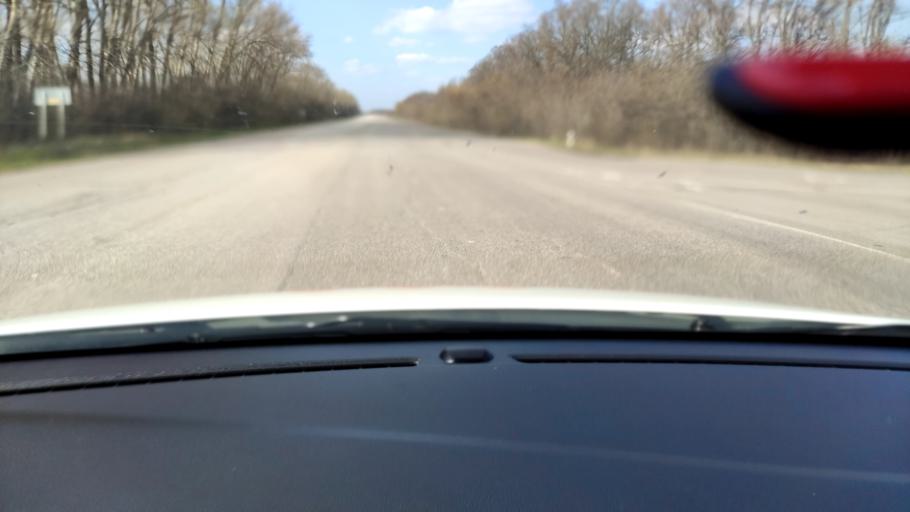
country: RU
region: Voronezj
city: Kolodeznyy
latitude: 51.2568
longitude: 39.0529
